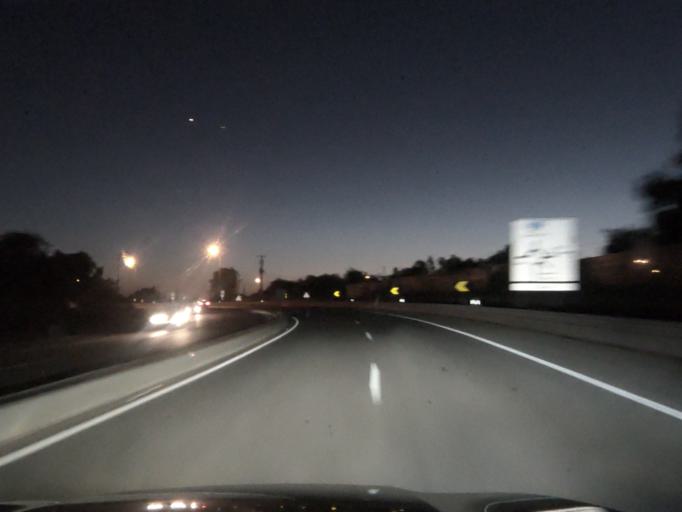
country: PT
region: Faro
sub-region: Loule
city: Loule
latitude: 37.1456
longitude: -8.0395
